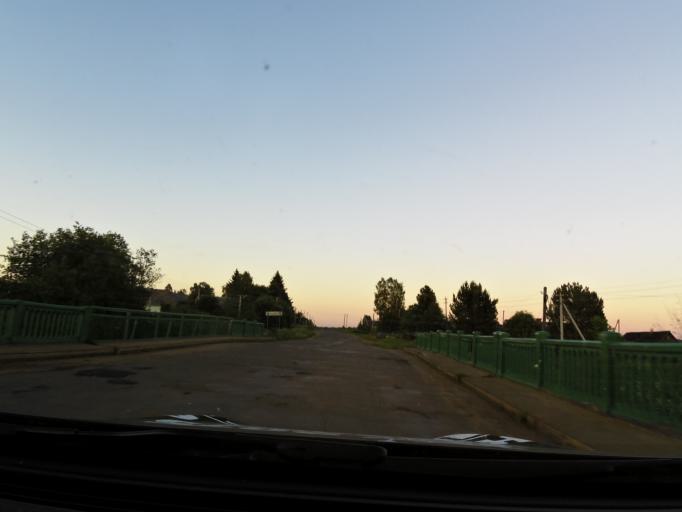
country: RU
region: Leningrad
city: Voznesen'ye
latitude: 60.8497
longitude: 35.5721
